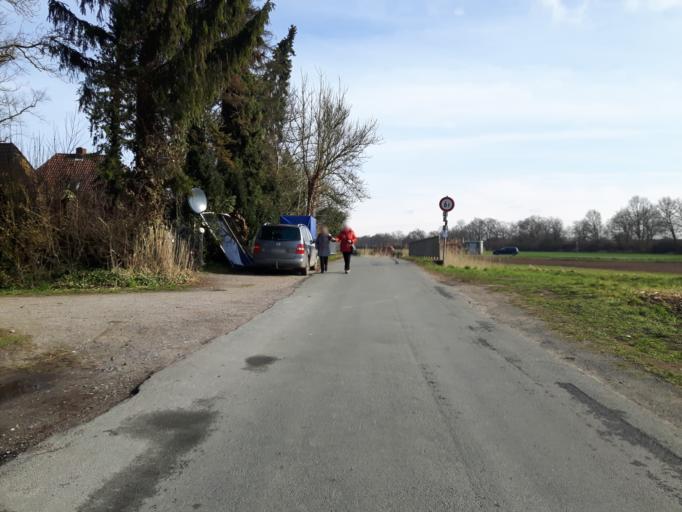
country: DE
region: North Rhine-Westphalia
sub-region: Regierungsbezirk Munster
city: Dulmen
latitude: 51.8046
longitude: 7.2627
